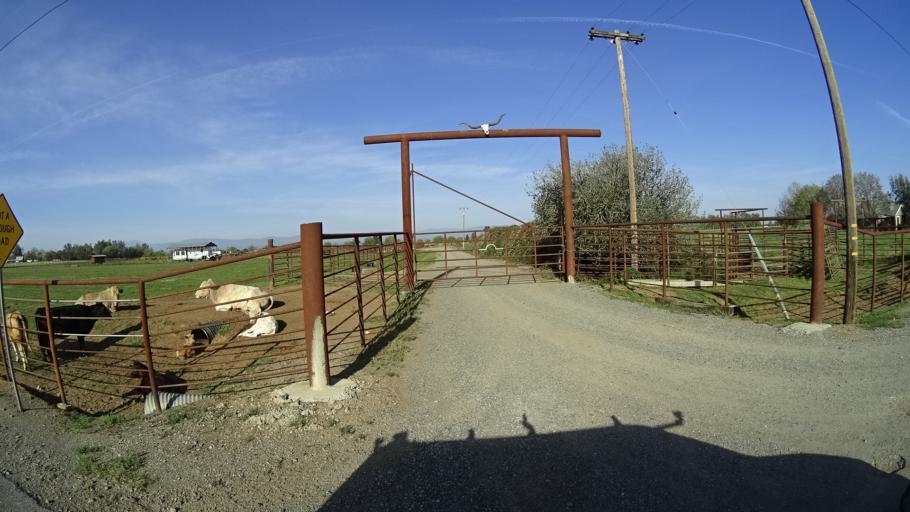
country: US
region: California
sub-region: Glenn County
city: Orland
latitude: 39.7151
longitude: -122.2347
